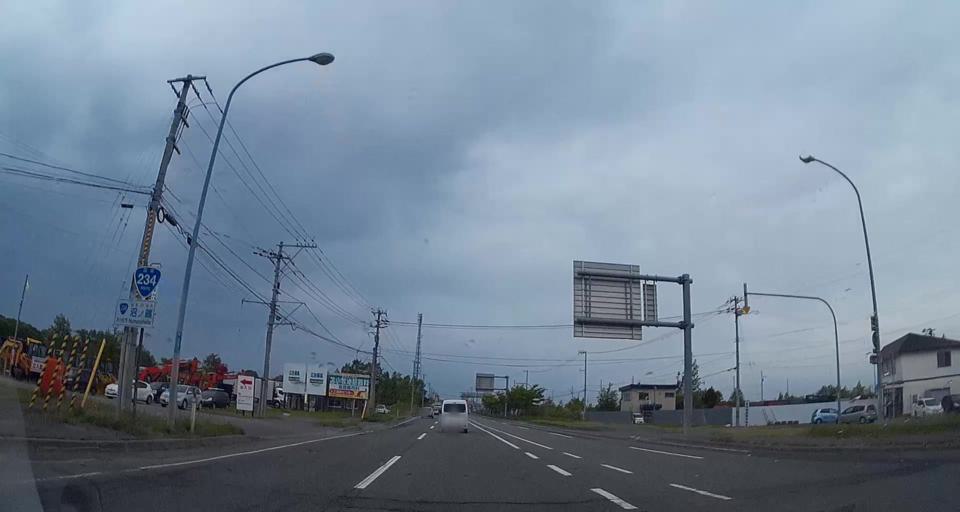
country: JP
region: Hokkaido
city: Tomakomai
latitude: 42.6760
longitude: 141.7096
